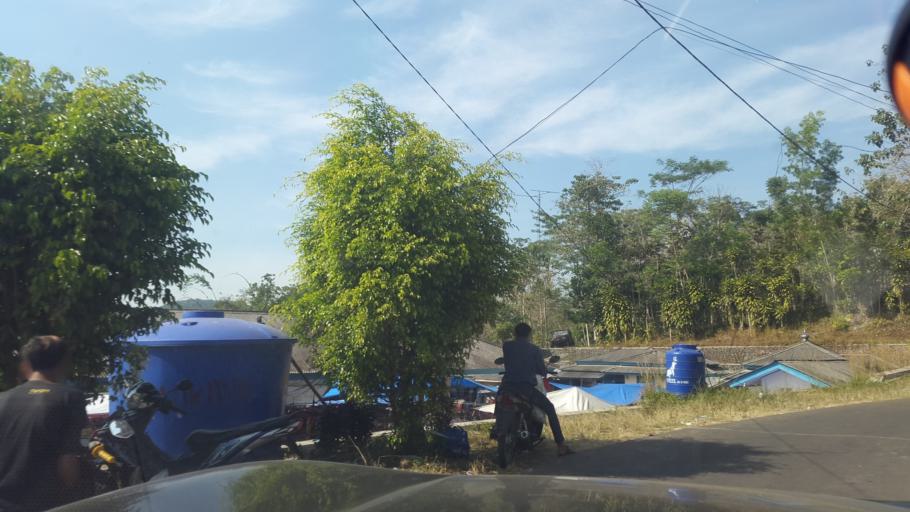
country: ID
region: West Java
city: Bojonggaling
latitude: -6.8963
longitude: 106.6465
